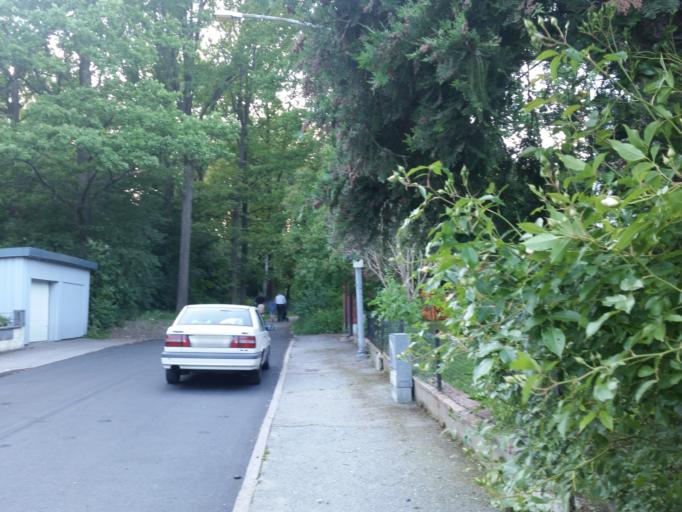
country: SE
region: Stockholm
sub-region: Solna Kommun
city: Rasunda
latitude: 59.3647
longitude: 17.9880
